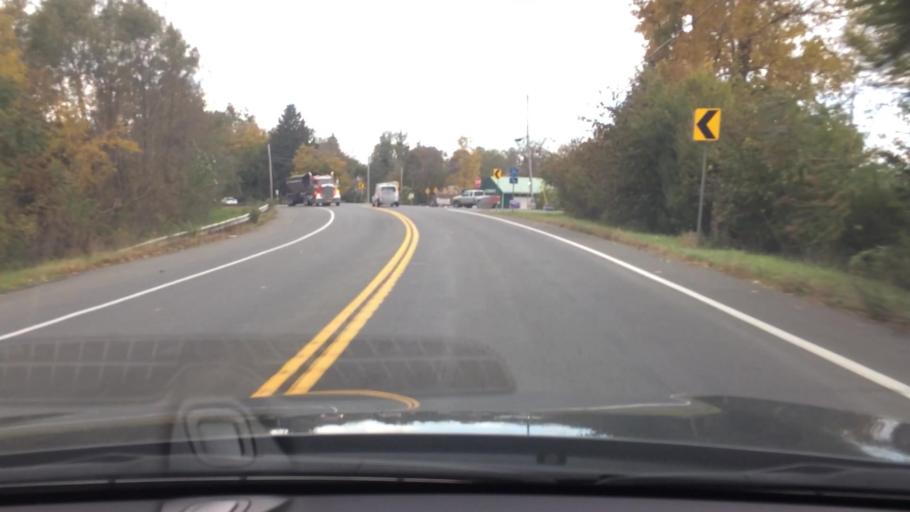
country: US
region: New York
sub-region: Columbia County
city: Oakdale
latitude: 42.1938
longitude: -73.7509
